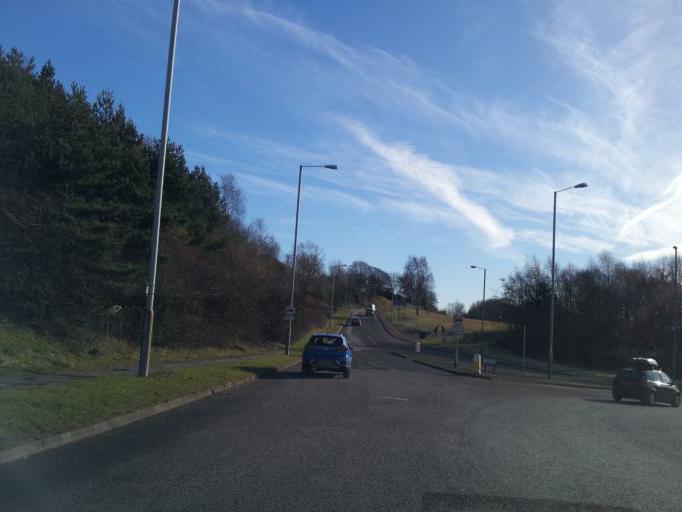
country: GB
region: England
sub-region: Staffordshire
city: Kidsgrove
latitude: 53.0620
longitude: -2.2223
